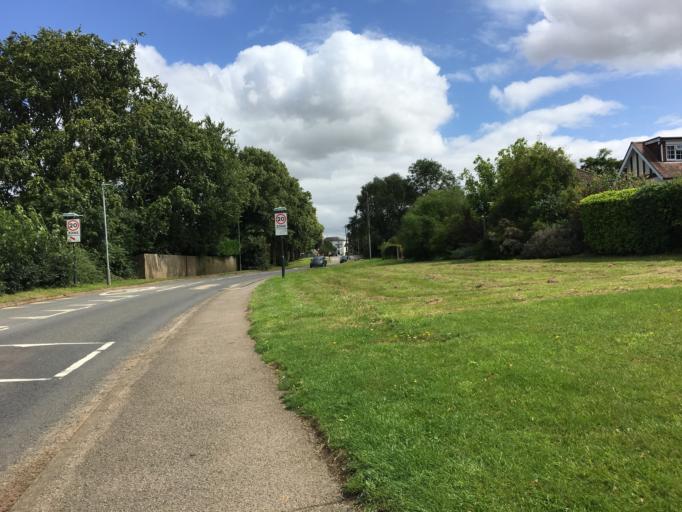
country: GB
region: England
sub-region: Warwickshire
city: Rugby
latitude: 52.3818
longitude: -1.2279
